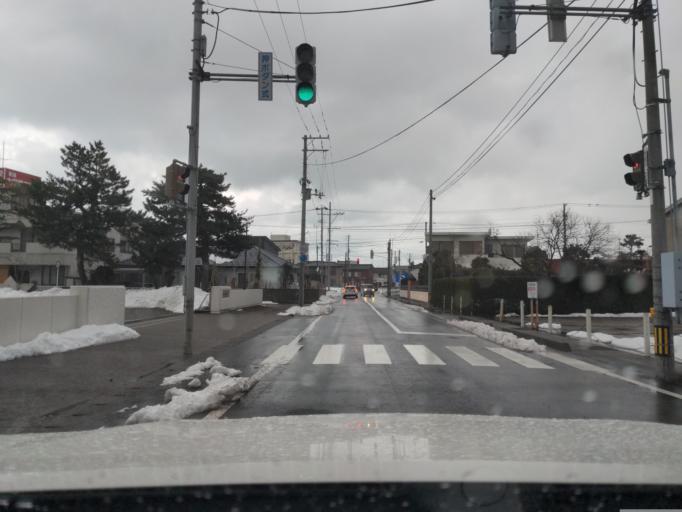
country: JP
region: Niigata
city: Kashiwazaki
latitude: 37.3687
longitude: 138.5713
